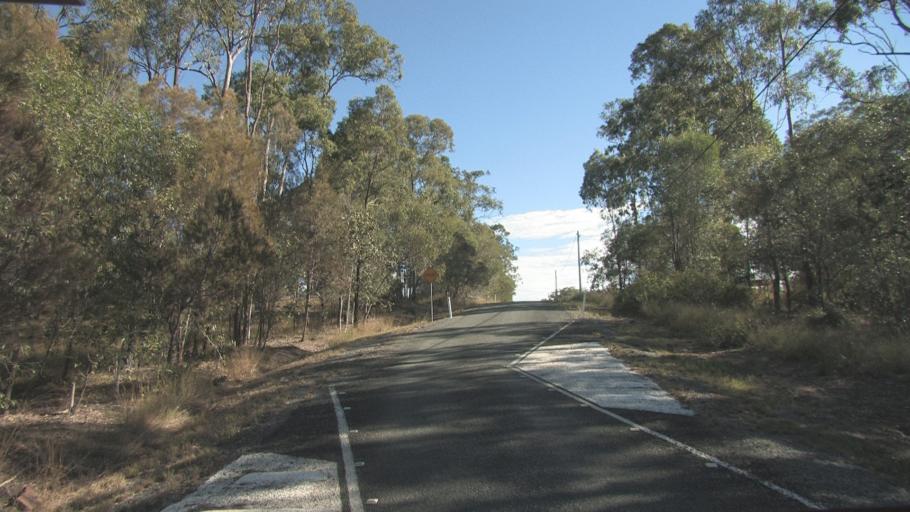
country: AU
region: Queensland
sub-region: Logan
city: Chambers Flat
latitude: -27.7972
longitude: 153.0818
